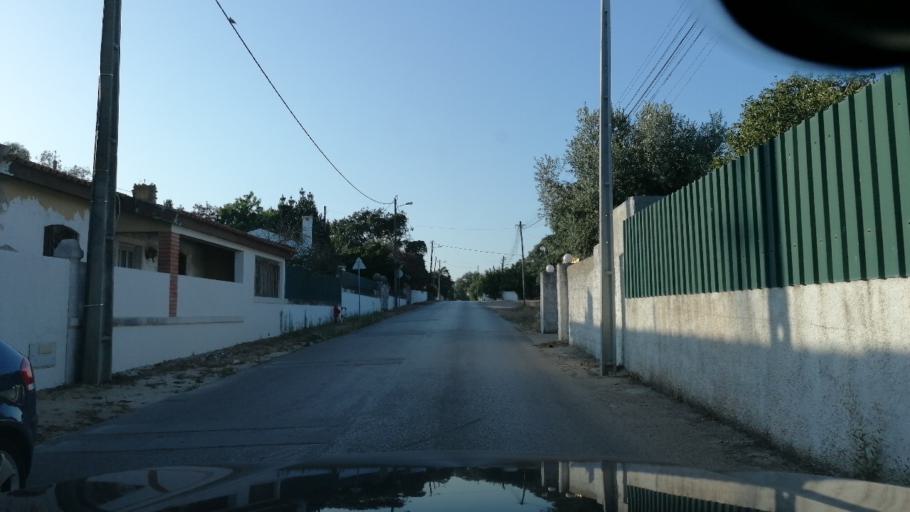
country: PT
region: Setubal
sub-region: Setubal
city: Setubal
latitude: 38.5447
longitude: -8.8396
